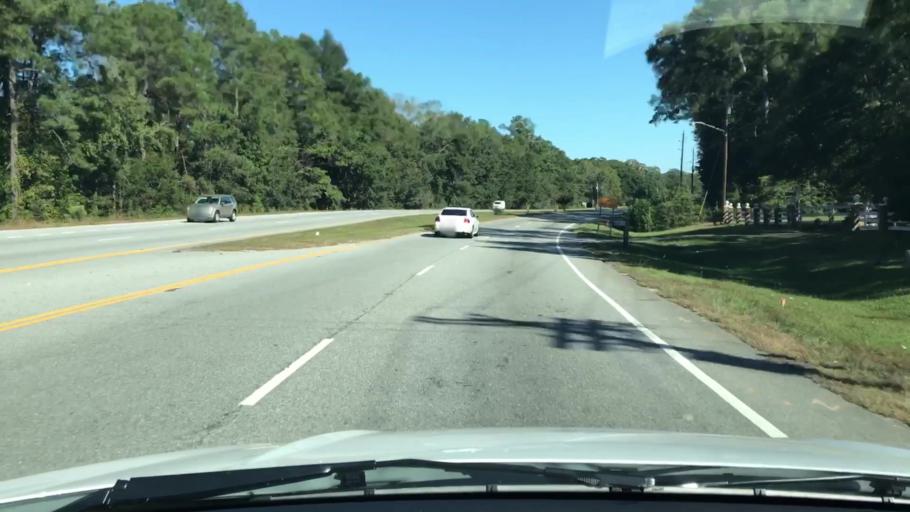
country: US
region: South Carolina
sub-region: Charleston County
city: Ravenel
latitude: 32.7834
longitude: -80.2095
